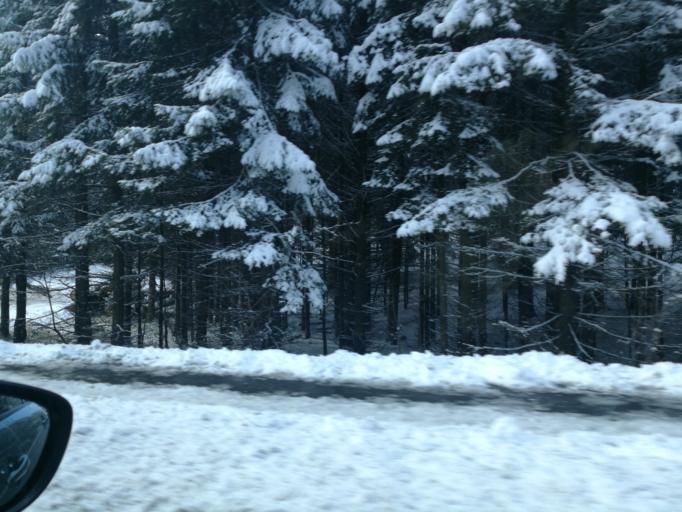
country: RO
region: Brasov
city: Brasov
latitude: 45.5966
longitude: 25.5528
